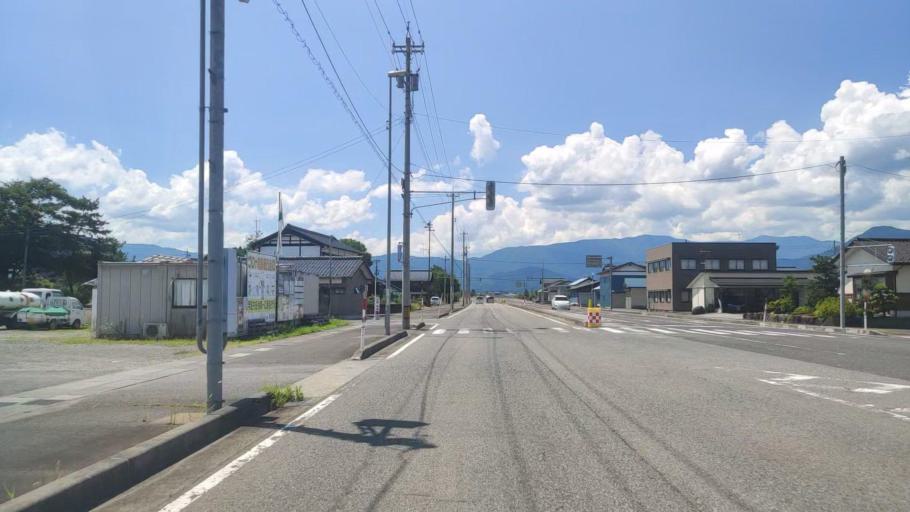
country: JP
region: Fukui
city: Ono
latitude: 36.0037
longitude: 136.5091
